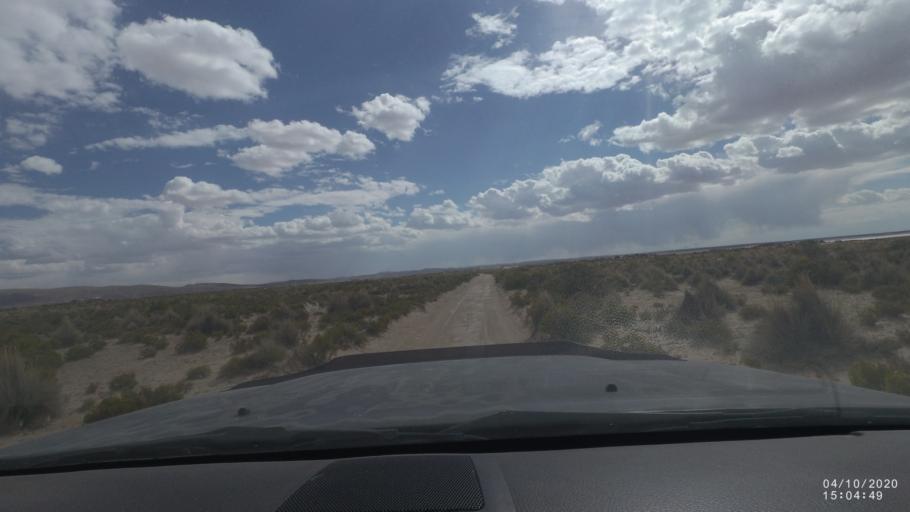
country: BO
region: Oruro
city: Poopo
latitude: -18.6909
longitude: -67.5524
